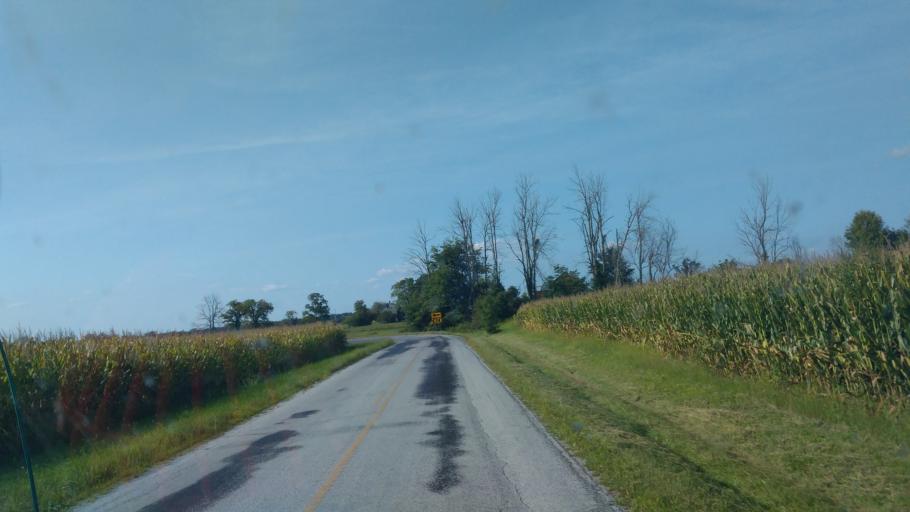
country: US
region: Ohio
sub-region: Hardin County
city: Kenton
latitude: 40.7337
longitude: -83.5747
